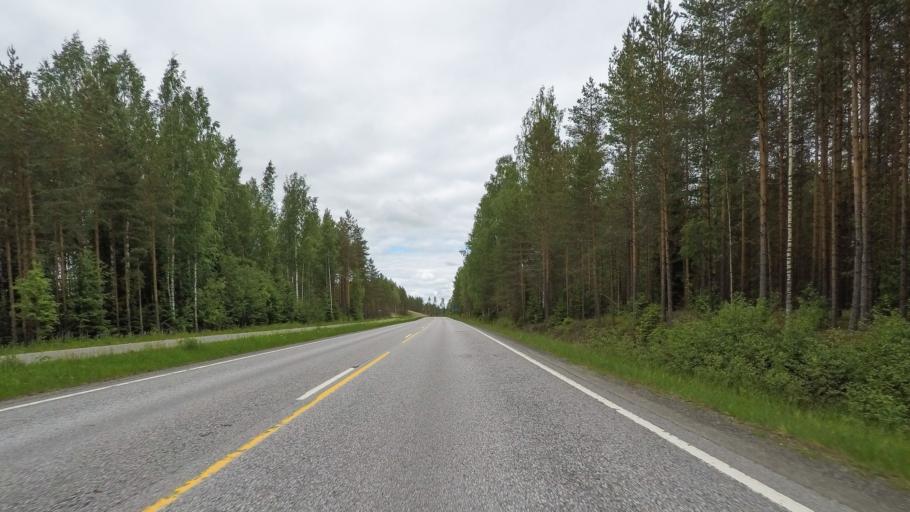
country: FI
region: Central Finland
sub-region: Jyvaeskylae
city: Toivakka
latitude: 62.0757
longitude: 26.0440
